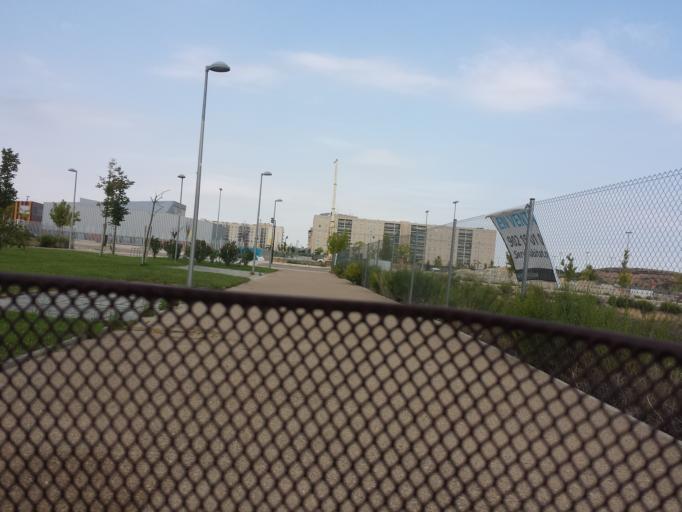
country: ES
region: Aragon
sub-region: Provincia de Zaragoza
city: Montecanal
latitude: 41.6248
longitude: -0.9559
